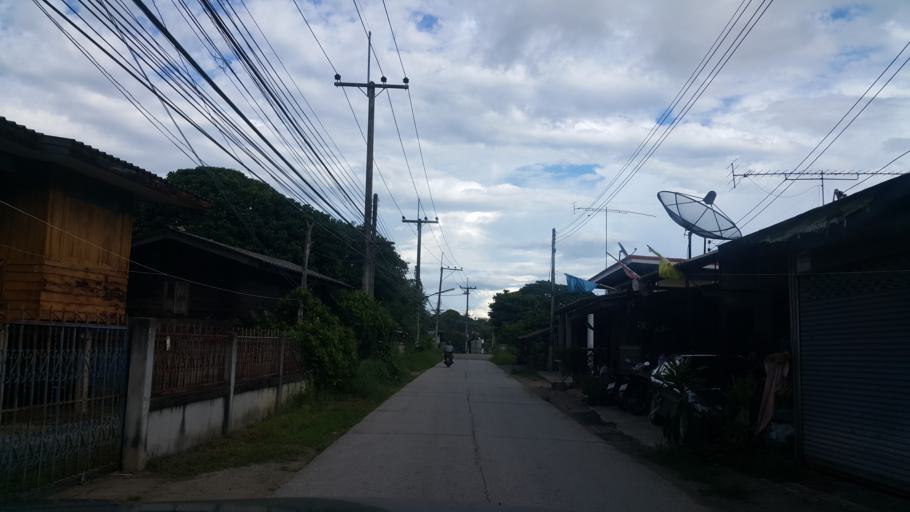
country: TH
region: Tak
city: Sam Ngao
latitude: 17.2399
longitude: 99.0288
